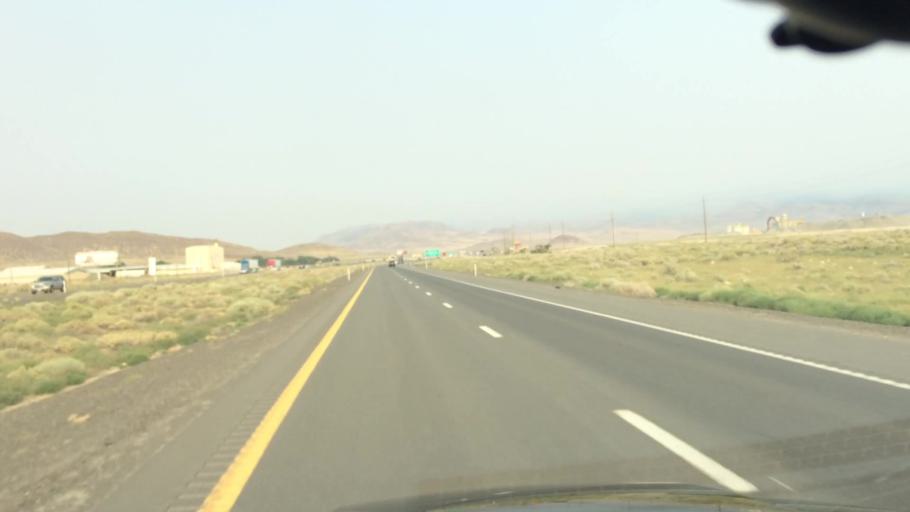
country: US
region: Nevada
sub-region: Lyon County
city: Fernley
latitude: 39.6153
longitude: -119.2517
